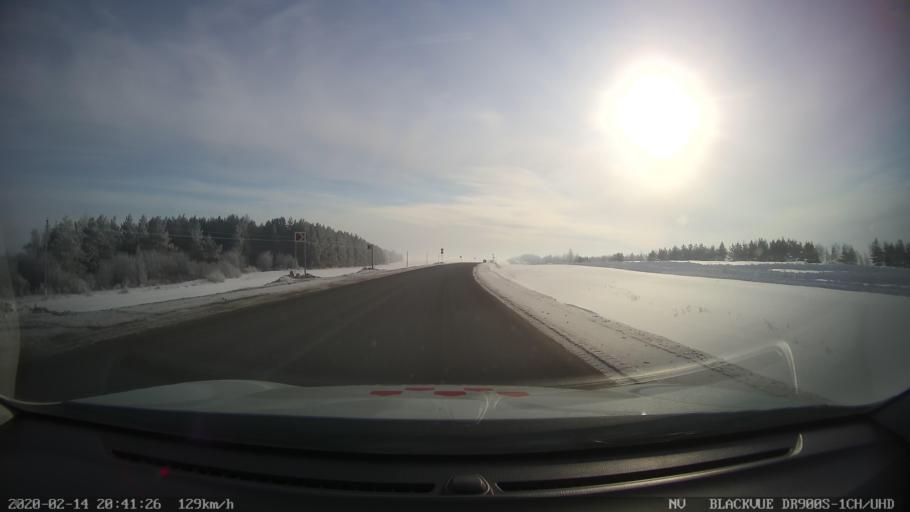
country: RU
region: Tatarstan
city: Kuybyshevskiy Zaton
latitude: 55.3305
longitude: 49.1196
